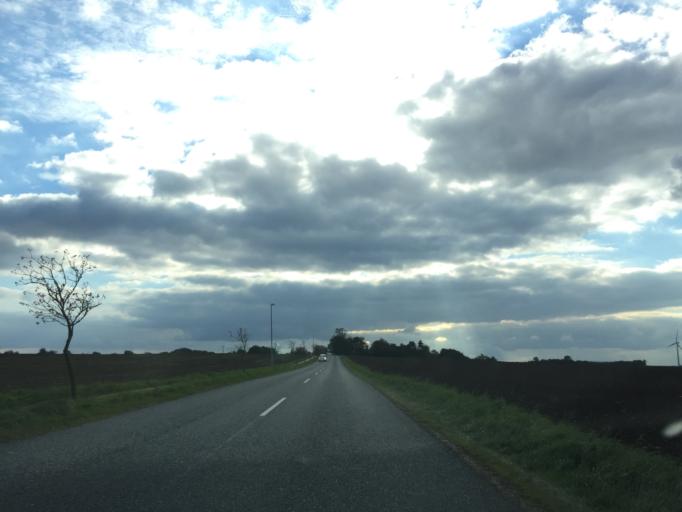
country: DK
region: Central Jutland
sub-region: Viborg Kommune
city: Bjerringbro
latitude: 56.2600
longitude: 9.7146
